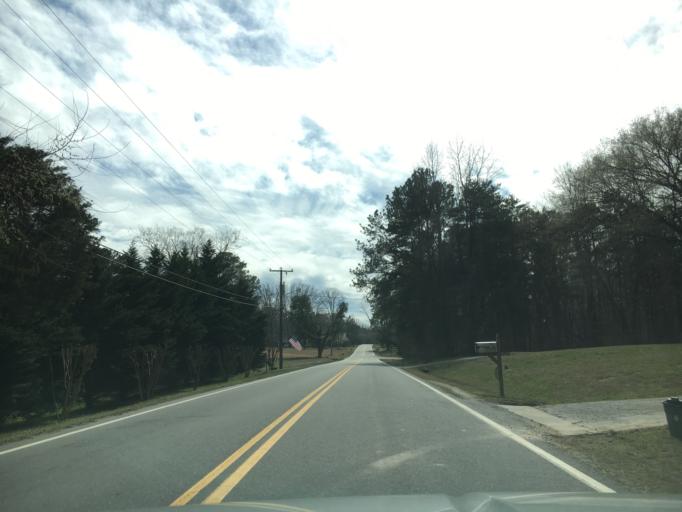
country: US
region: Virginia
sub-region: Halifax County
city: Halifax
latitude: 36.7555
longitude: -78.9160
